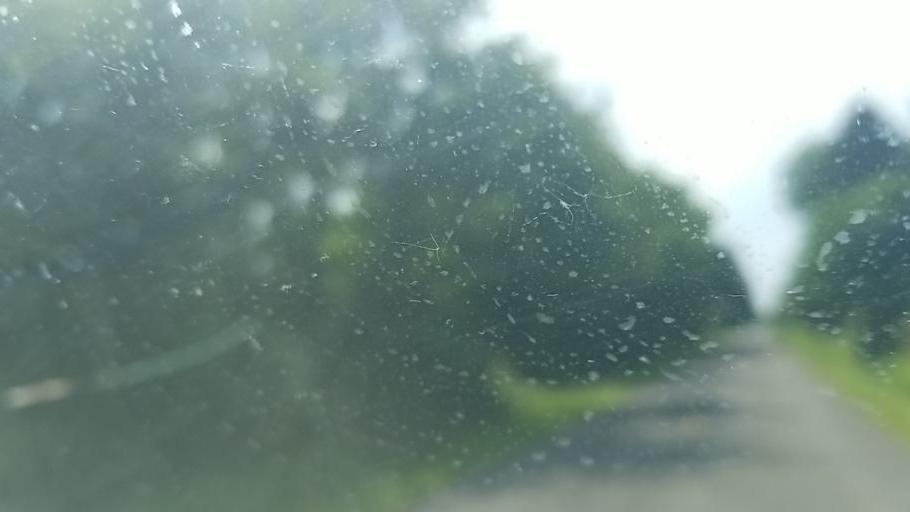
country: US
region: Ohio
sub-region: Medina County
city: Lodi
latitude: 41.0899
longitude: -81.9692
